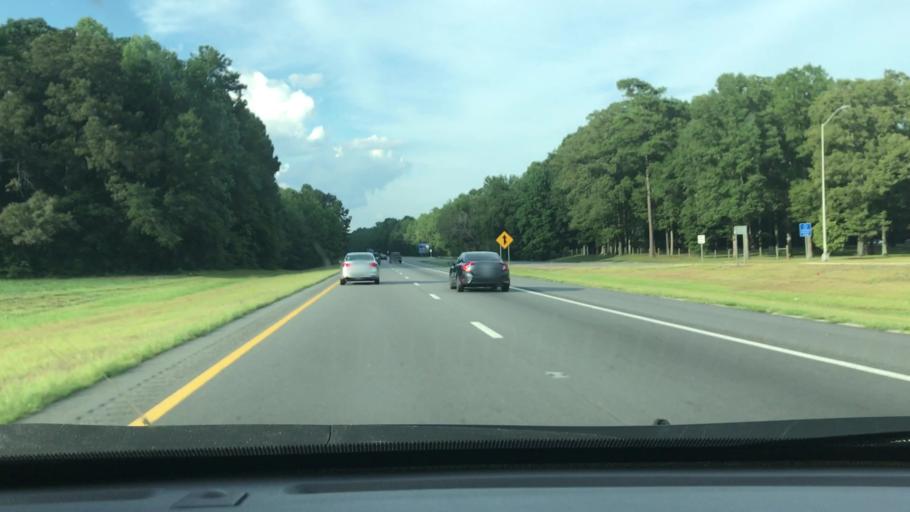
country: US
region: North Carolina
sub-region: Cumberland County
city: Vander
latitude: 34.9966
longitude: -78.8297
